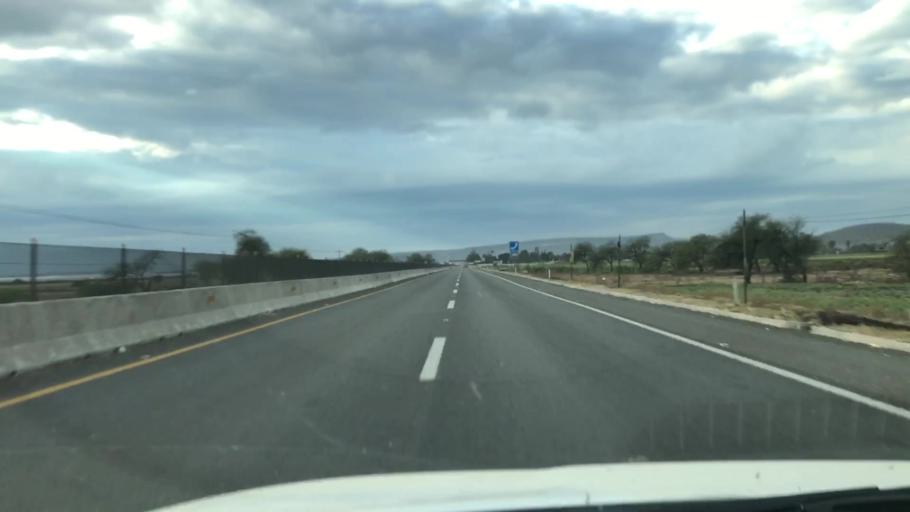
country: MX
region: Guanajuato
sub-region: Penjamo
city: Estacion la Piedad
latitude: 20.3859
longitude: -101.9107
